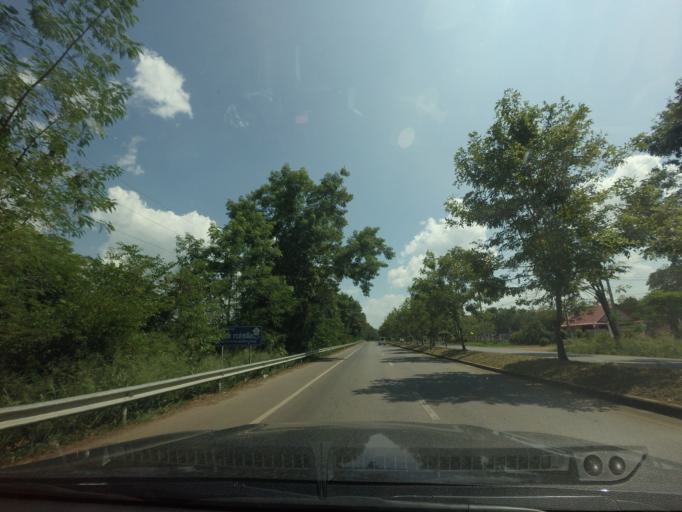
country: TH
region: Phetchabun
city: Nong Phai
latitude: 16.0494
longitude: 101.0794
